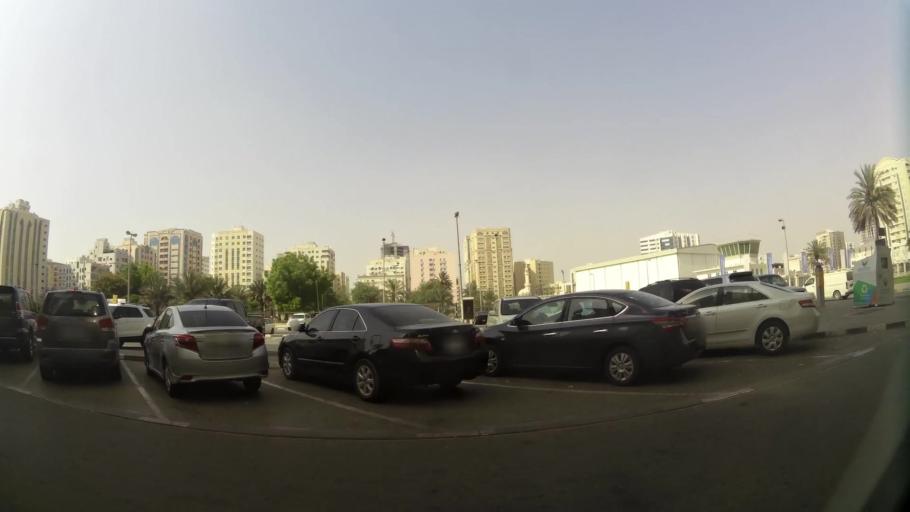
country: AE
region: Ash Shariqah
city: Sharjah
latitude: 25.3456
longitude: 55.3943
